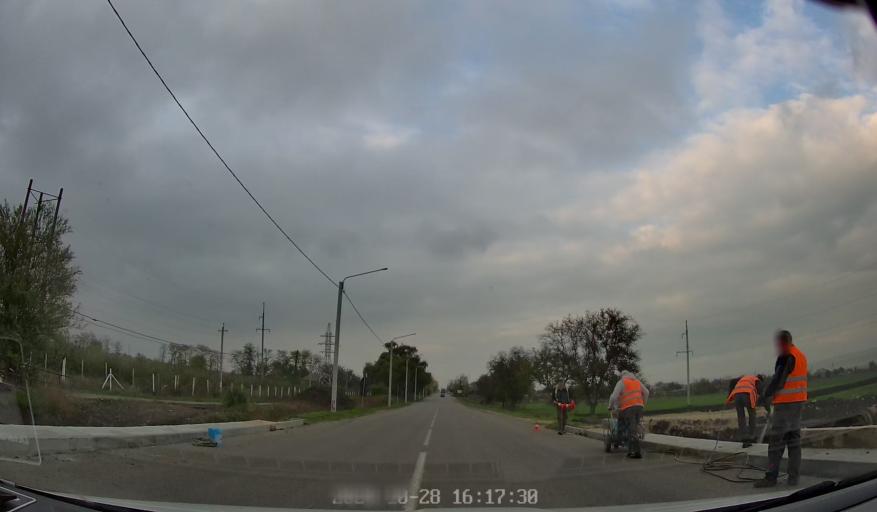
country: MD
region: Straseni
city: Taraclia
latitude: 45.9999
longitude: 28.5673
